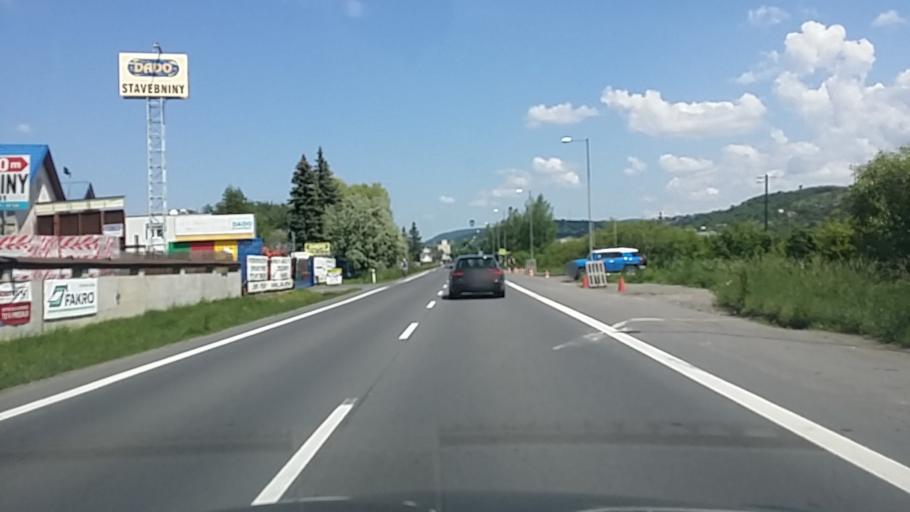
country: SK
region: Banskobystricky
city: Krupina
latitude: 48.3374
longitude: 19.0643
